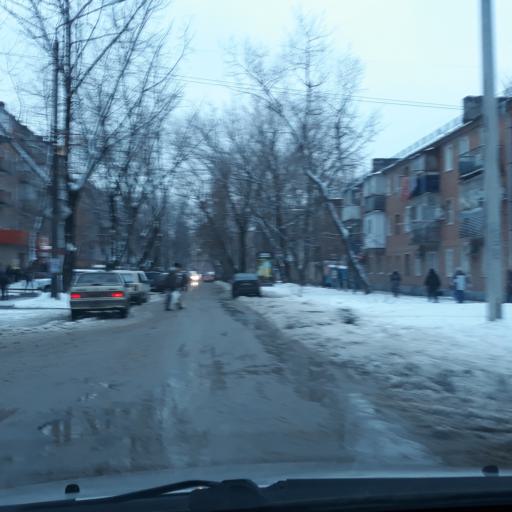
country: RU
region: Rostov
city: Taganrog
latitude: 47.2407
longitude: 38.8832
